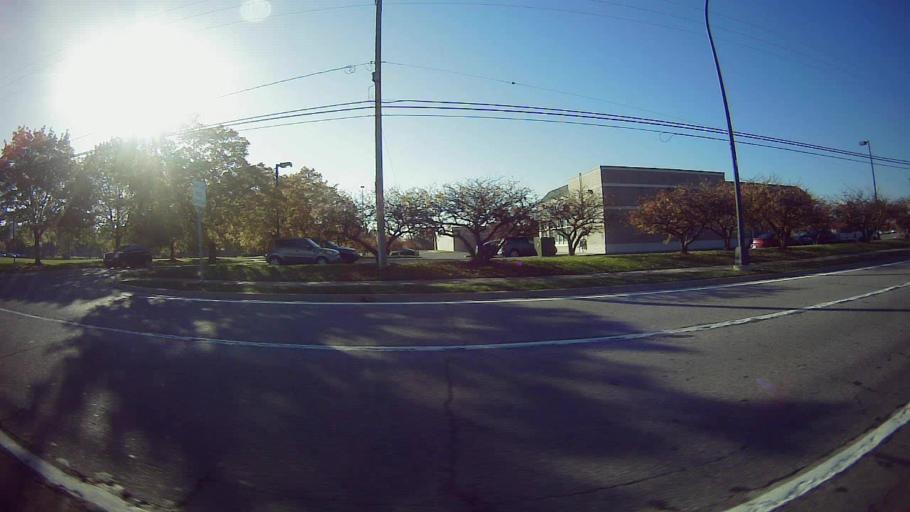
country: US
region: Michigan
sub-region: Wayne County
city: Dearborn
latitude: 42.3290
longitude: -83.2045
